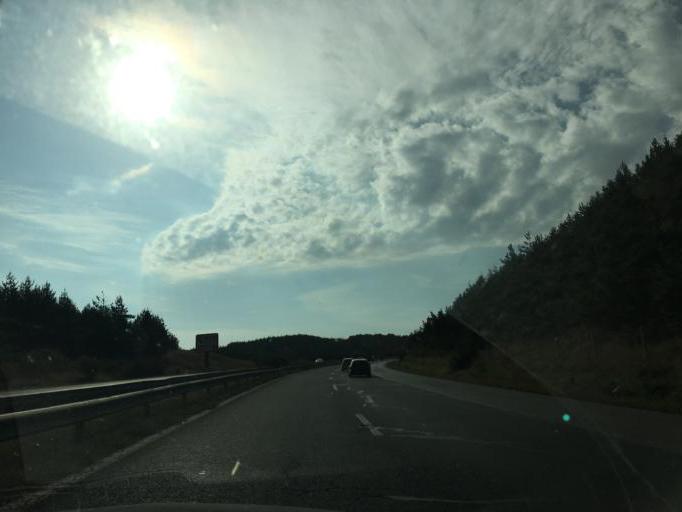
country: BG
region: Sofiya
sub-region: Obshtina Elin Pelin
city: Elin Pelin
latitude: 42.5810
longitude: 23.6519
